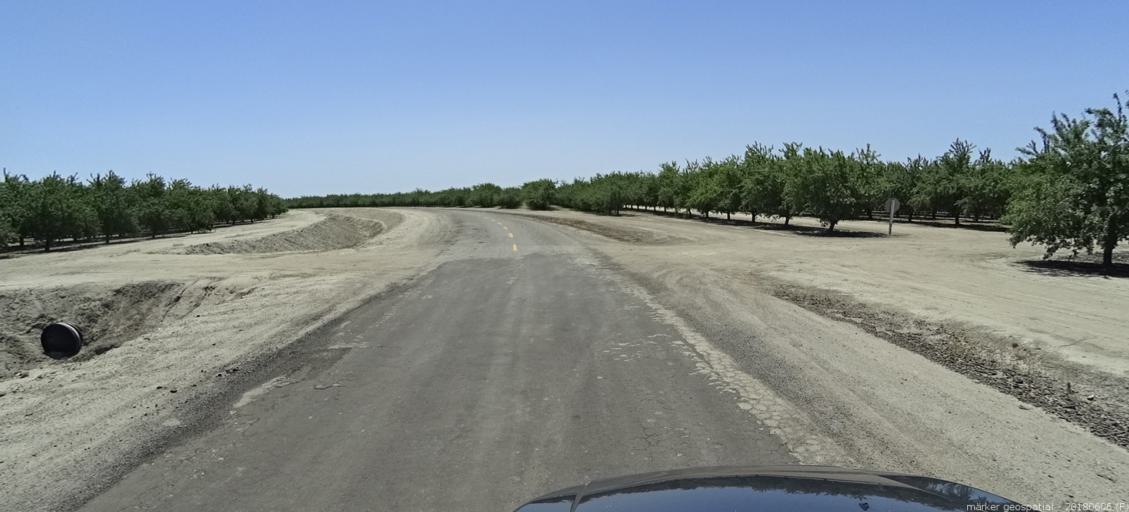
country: US
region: California
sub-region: Fresno County
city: Mendota
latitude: 36.8298
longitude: -120.3766
